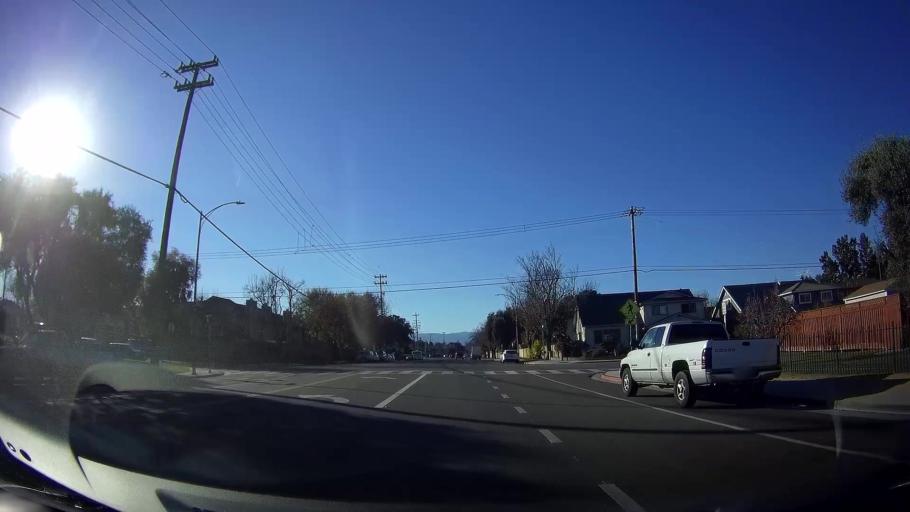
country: US
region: California
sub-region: Santa Clara County
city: Campbell
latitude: 37.3014
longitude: -121.9612
